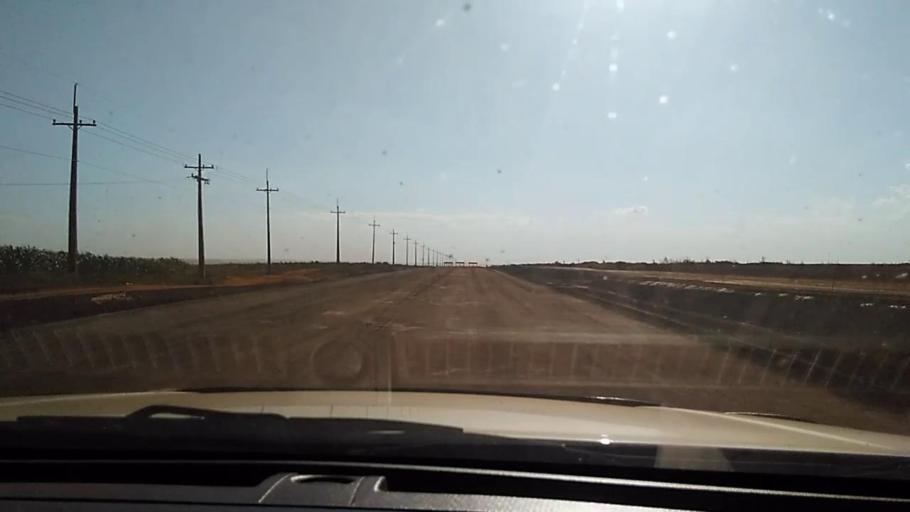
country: PY
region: Alto Parana
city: Naranjal
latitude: -25.9183
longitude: -55.4278
